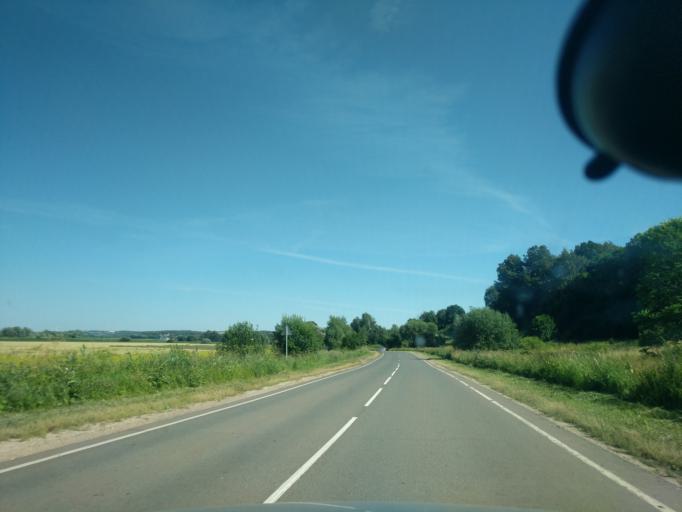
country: RU
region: Moskovskaya
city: Serpukhov
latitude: 54.8514
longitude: 37.4902
